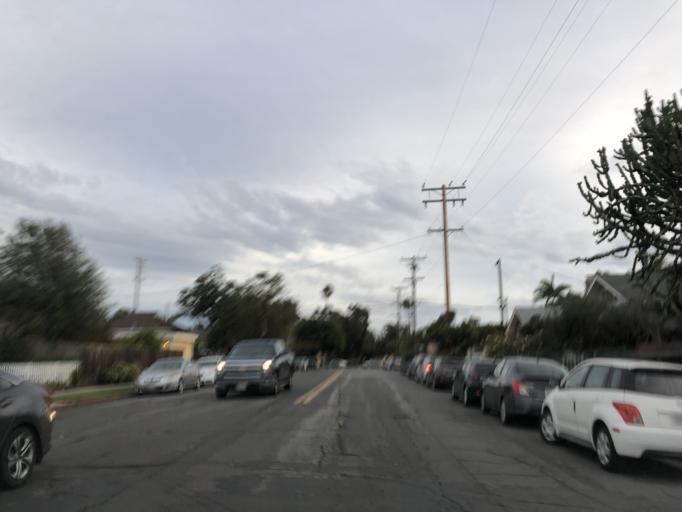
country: US
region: California
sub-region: San Diego County
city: San Diego
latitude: 32.7476
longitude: -117.1553
